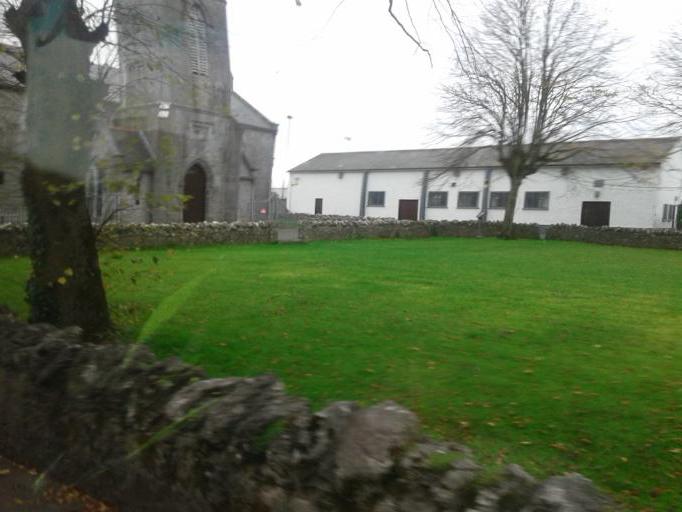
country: IE
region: Munster
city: Nenagh Bridge
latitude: 52.9428
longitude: -8.0395
